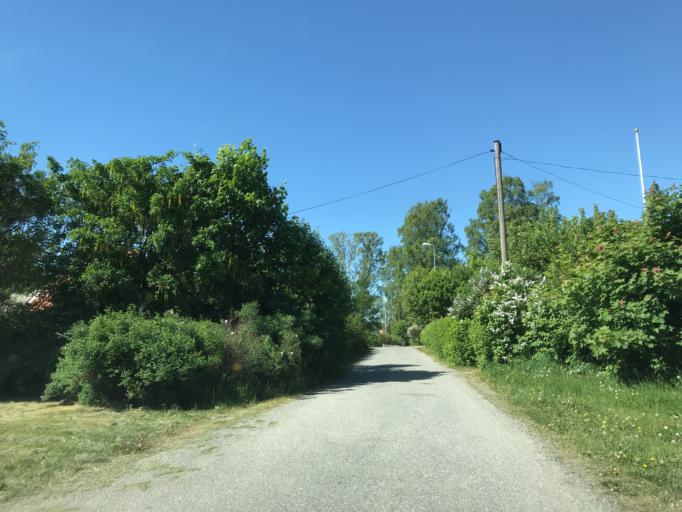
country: SE
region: Stockholm
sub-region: Sollentuna Kommun
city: Sollentuna
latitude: 59.4196
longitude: 17.9640
